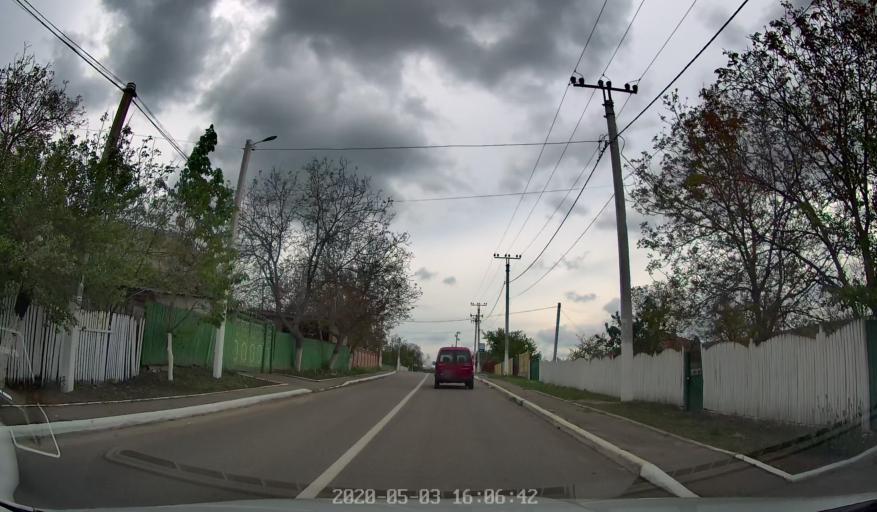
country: MD
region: Calarasi
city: Calarasi
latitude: 47.1947
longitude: 28.3503
